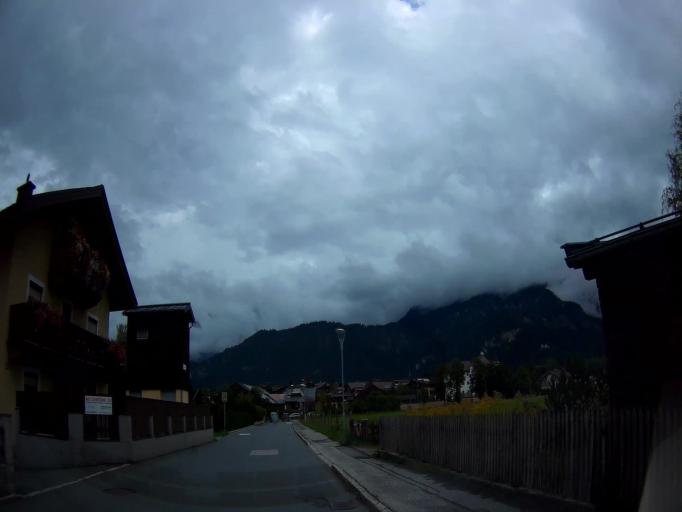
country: AT
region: Salzburg
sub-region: Politischer Bezirk Zell am See
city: Saalfelden am Steinernen Meer
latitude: 47.4298
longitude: 12.8334
